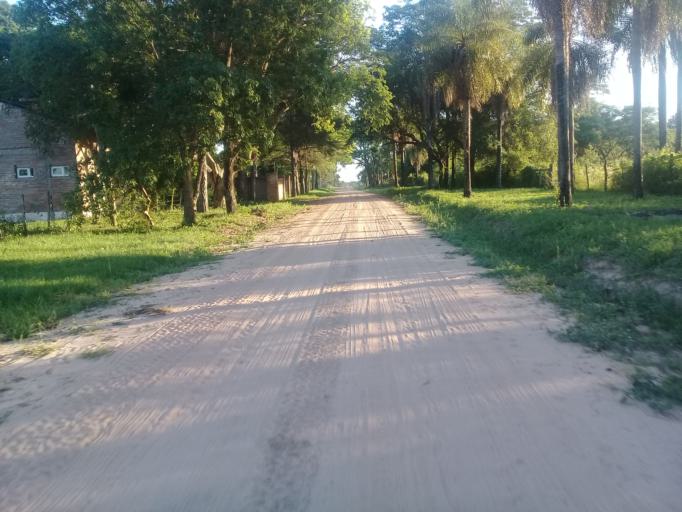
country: AR
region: Corrientes
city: San Luis del Palmar
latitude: -27.4689
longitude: -58.6637
